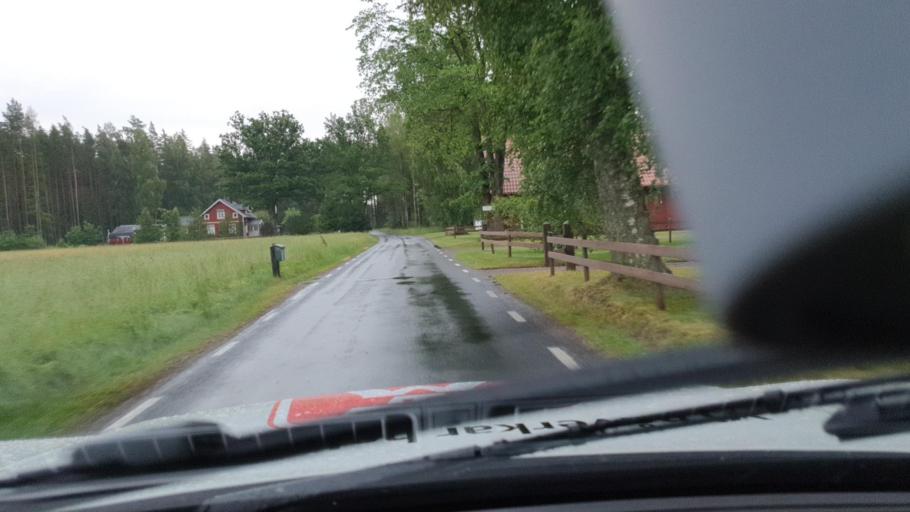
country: SE
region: Vaestra Goetaland
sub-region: Skovde Kommun
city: Stopen
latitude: 58.4540
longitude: 13.9220
